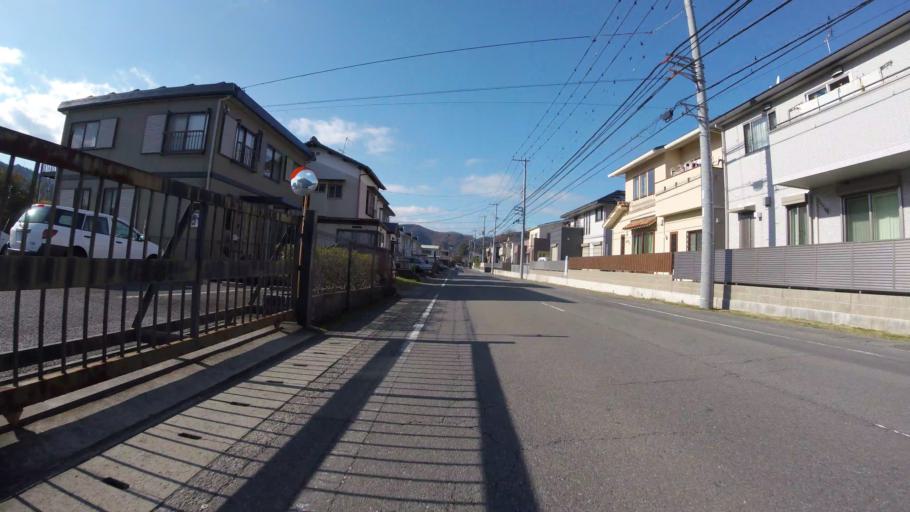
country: JP
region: Shizuoka
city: Mishima
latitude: 34.9919
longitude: 138.9475
